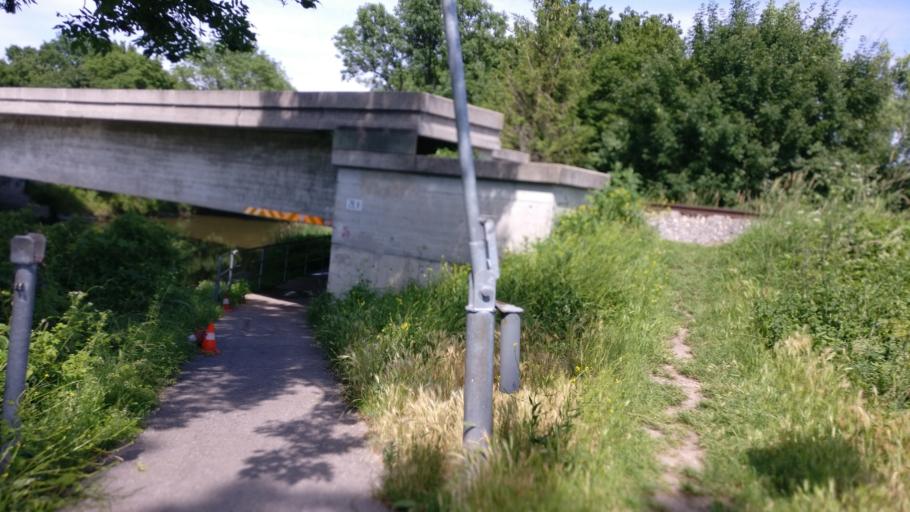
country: AT
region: Lower Austria
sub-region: Politischer Bezirk Baden
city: Trumau
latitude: 47.9852
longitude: 16.3332
